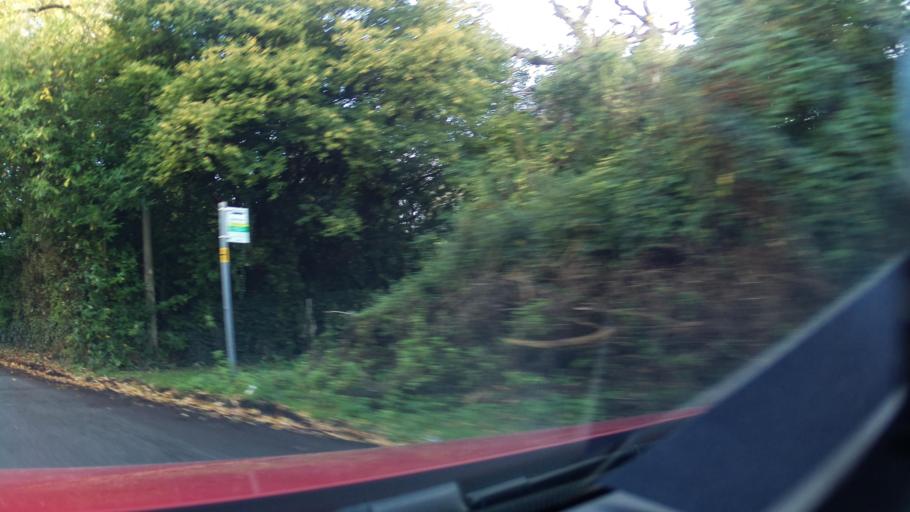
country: GB
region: England
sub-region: South Gloucestershire
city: Severn Beach
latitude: 51.5341
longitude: -2.6235
